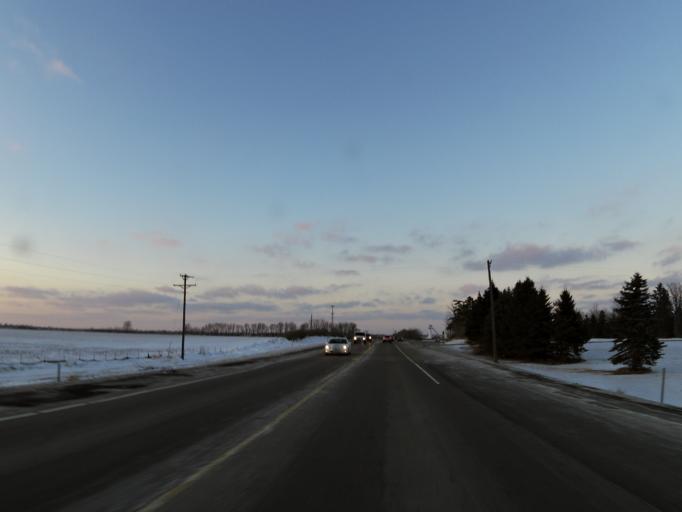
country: US
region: Minnesota
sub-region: Dakota County
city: Rosemount
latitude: 44.7064
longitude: -93.1365
